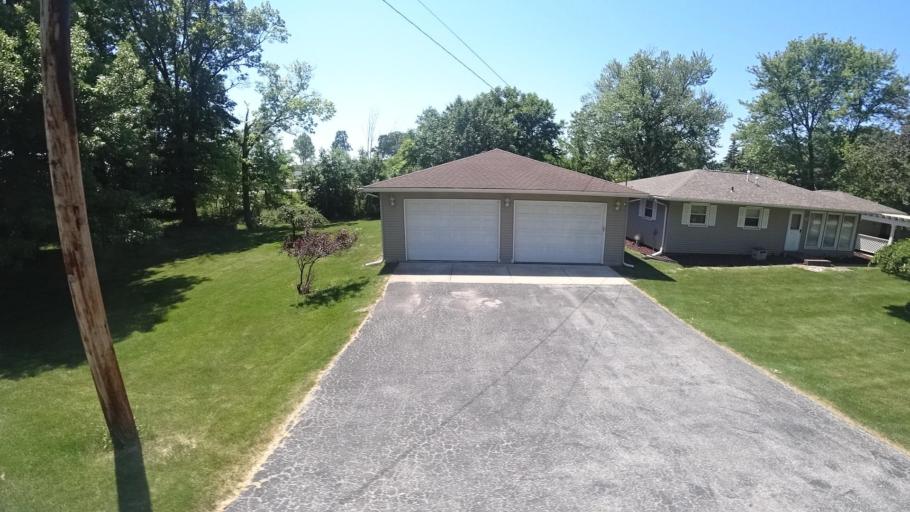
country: US
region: Indiana
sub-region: Porter County
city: Burns Harbor
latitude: 41.6068
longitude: -87.1350
